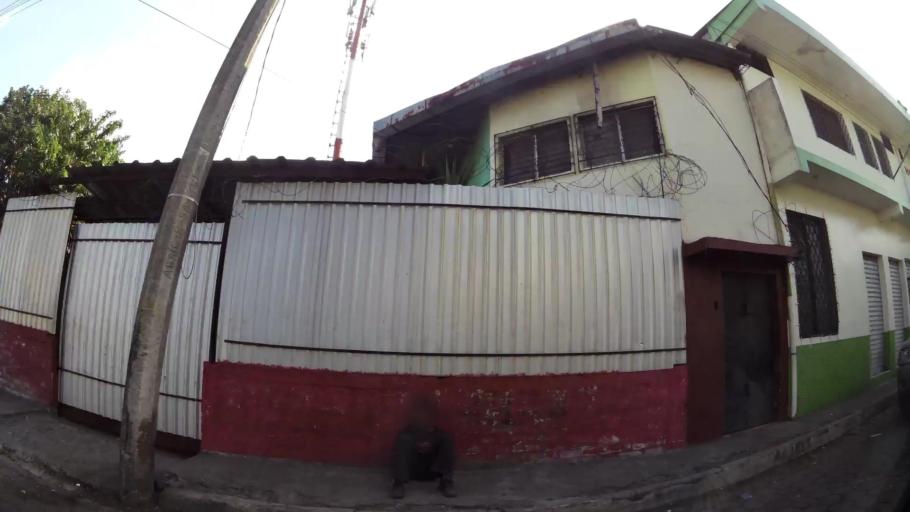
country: SV
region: San Salvador
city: San Salvador
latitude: 13.6994
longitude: -89.1765
